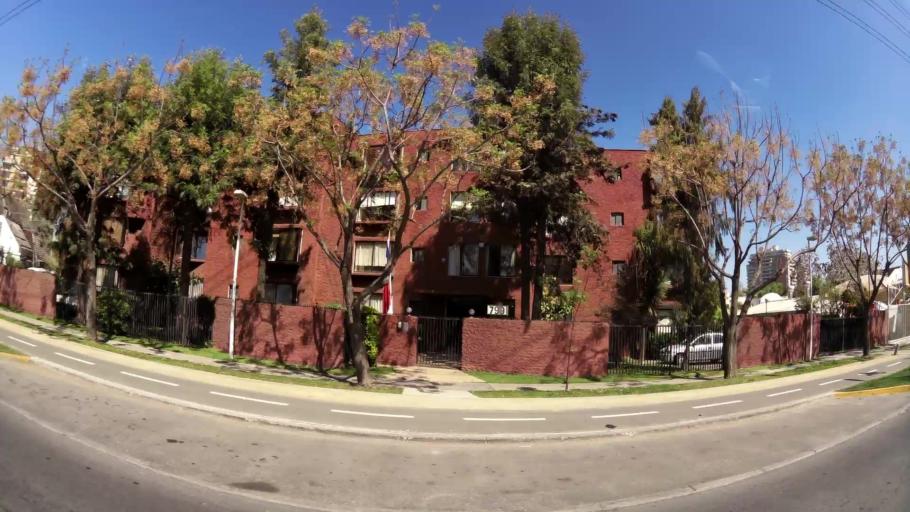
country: CL
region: Santiago Metropolitan
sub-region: Provincia de Santiago
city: Villa Presidente Frei, Nunoa, Santiago, Chile
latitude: -33.4155
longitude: -70.5563
